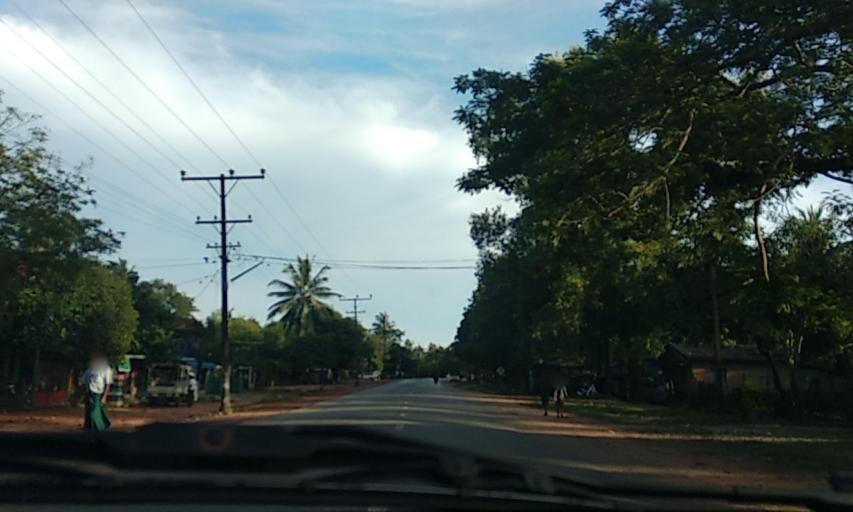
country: MM
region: Mon
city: Mawlamyine
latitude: 16.4072
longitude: 97.7014
